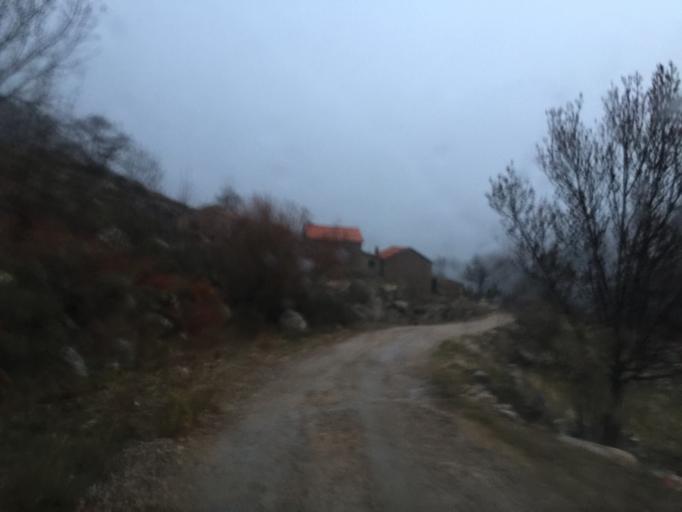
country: PT
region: Guarda
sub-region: Manteigas
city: Manteigas
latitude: 40.3798
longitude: -7.5488
